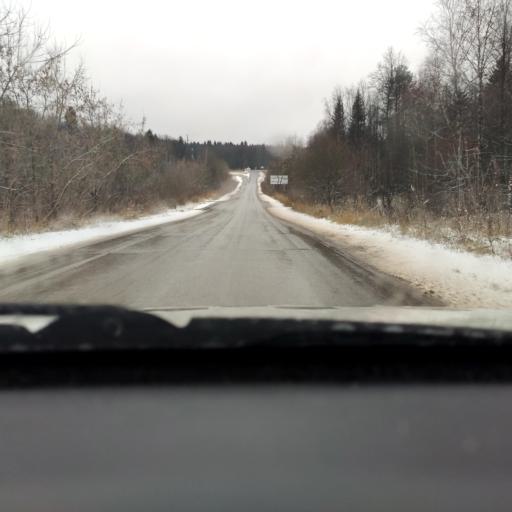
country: RU
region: Perm
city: Ferma
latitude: 57.9762
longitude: 56.3508
